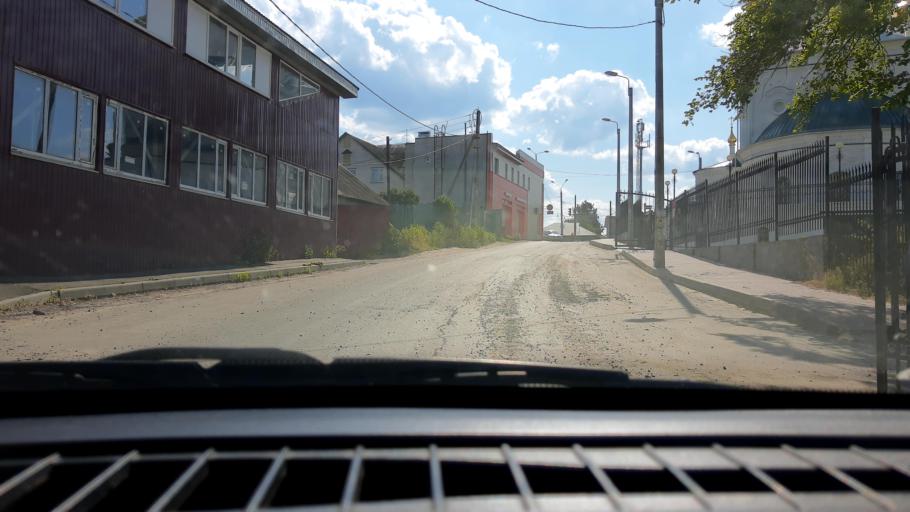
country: RU
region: Nizjnij Novgorod
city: Neklyudovo
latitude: 56.3807
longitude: 43.8331
